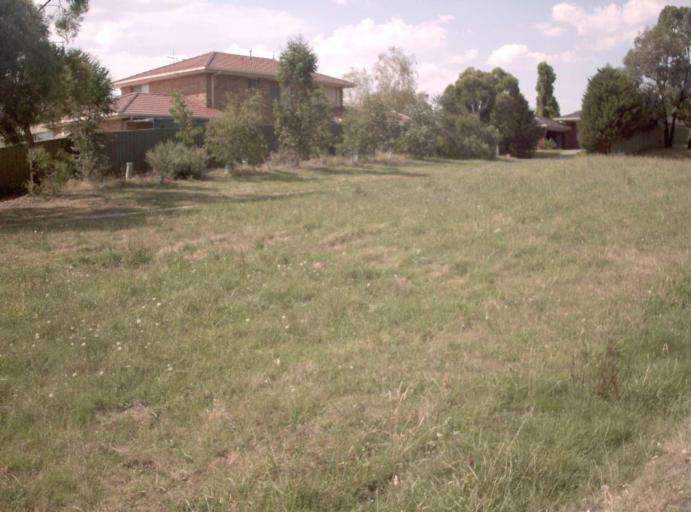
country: AU
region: Victoria
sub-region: Knox
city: Ferntree Gully
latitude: -37.9098
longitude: 145.2760
